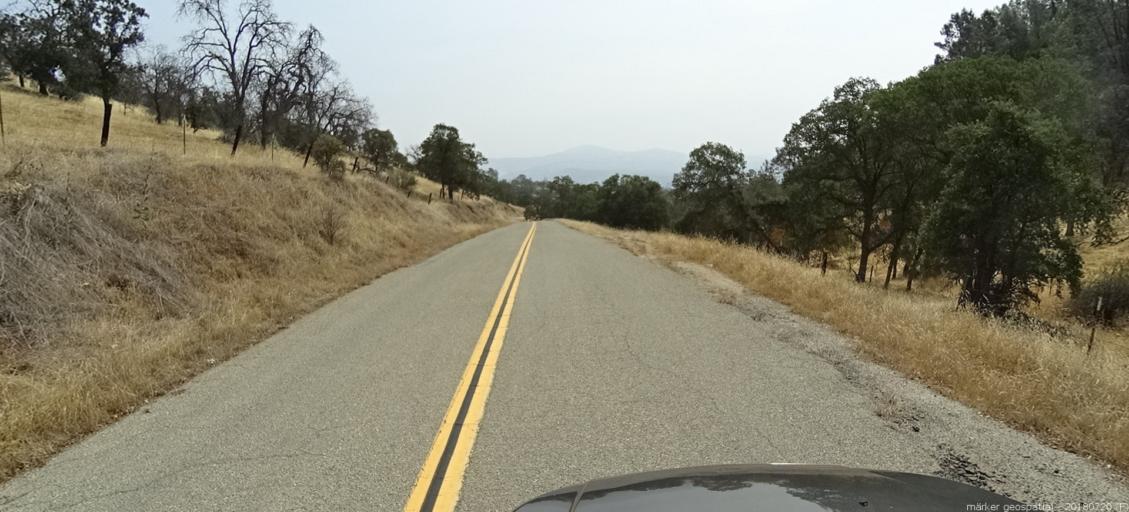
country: US
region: California
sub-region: Madera County
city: Yosemite Lakes
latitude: 37.2829
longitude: -119.8186
